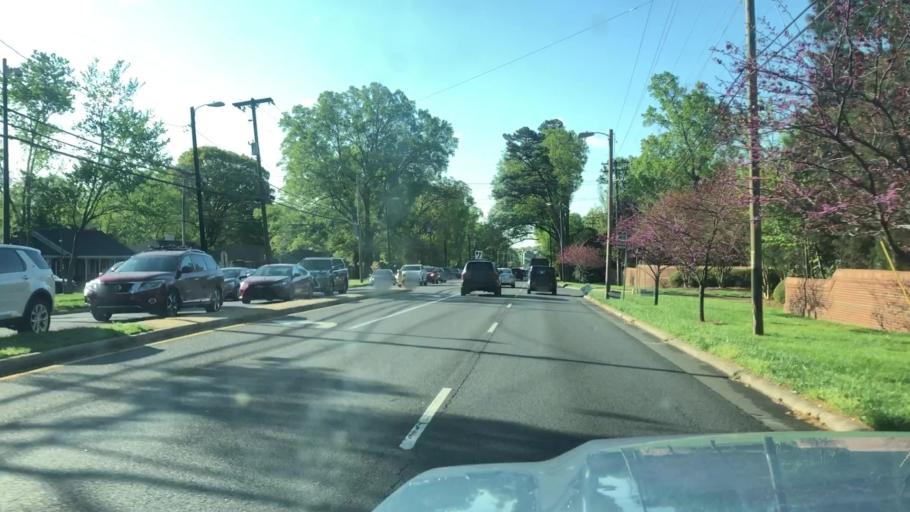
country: US
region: North Carolina
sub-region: Mecklenburg County
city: Charlotte
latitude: 35.1674
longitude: -80.8041
